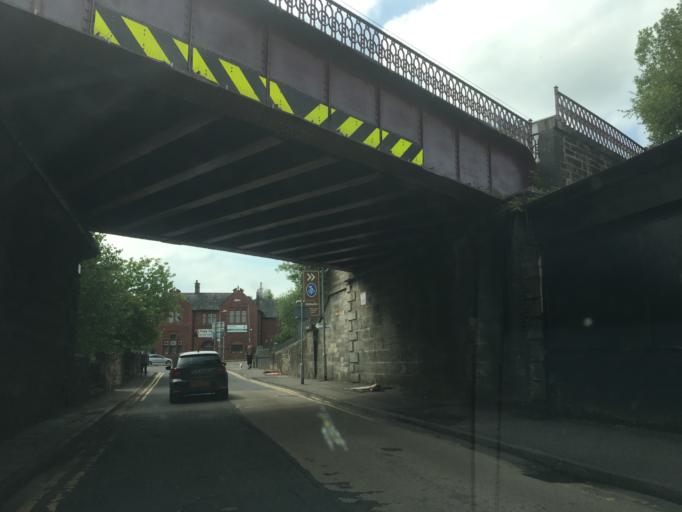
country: GB
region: Scotland
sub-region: North Lanarkshire
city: Coatbridge
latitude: 55.8624
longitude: -4.0298
